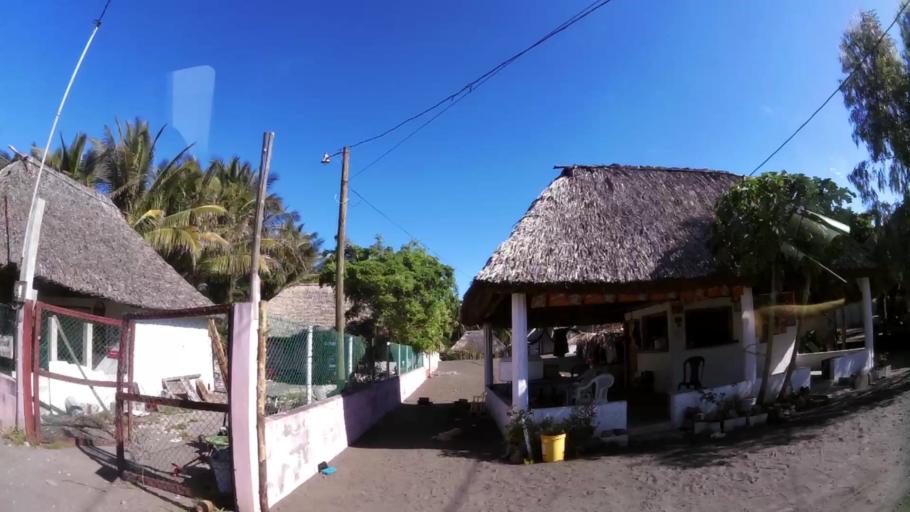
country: GT
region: Jutiapa
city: Pasaco
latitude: 13.8565
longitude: -90.3895
